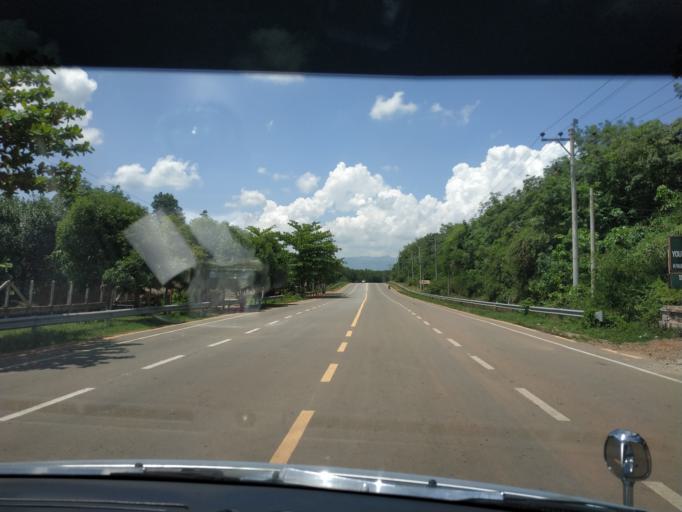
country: MM
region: Mon
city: Kyaikto
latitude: 17.3260
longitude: 97.0243
